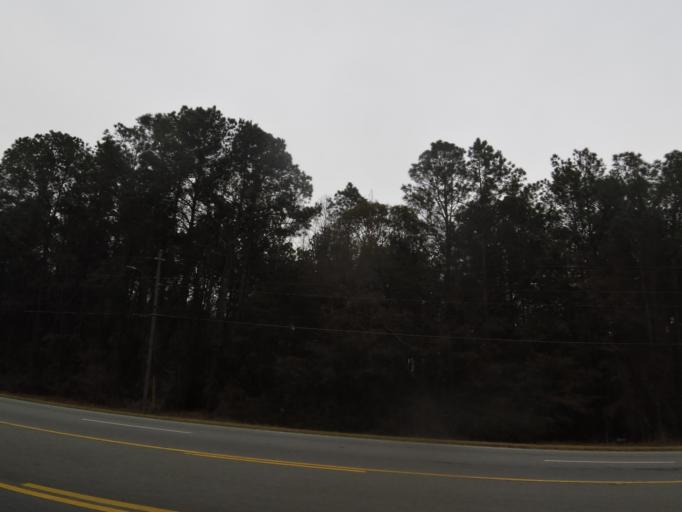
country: US
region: Georgia
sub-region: Grady County
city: Cairo
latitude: 30.8771
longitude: -84.1700
